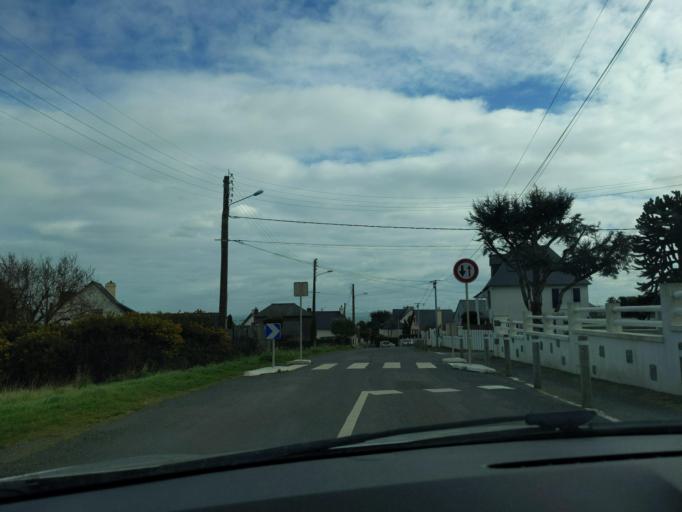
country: FR
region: Brittany
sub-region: Departement des Cotes-d'Armor
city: Saint-Quay-Portrieux
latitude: 48.6634
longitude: -2.8495
